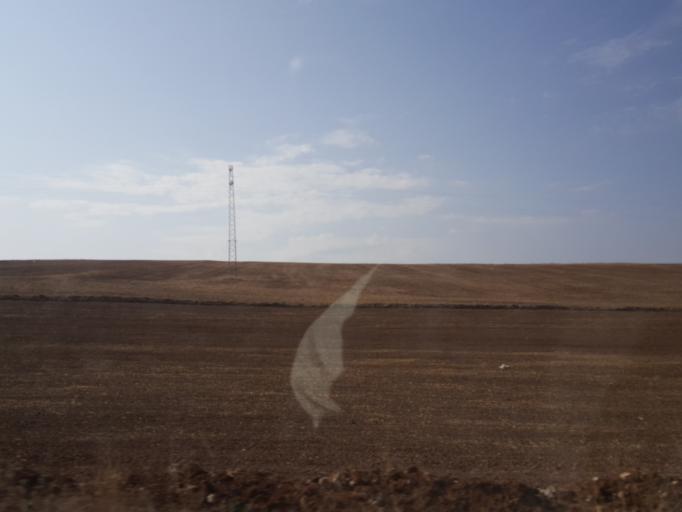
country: TR
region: Corum
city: Cemilbey
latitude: 40.1746
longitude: 35.0401
